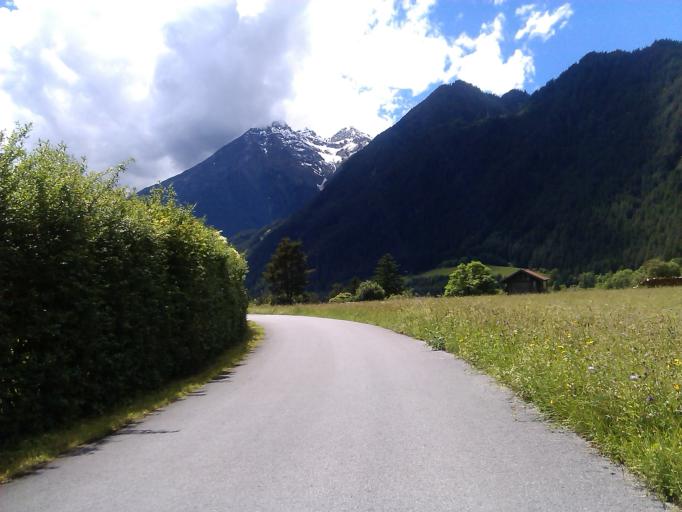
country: AT
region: Tyrol
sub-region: Politischer Bezirk Landeck
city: Pfunds
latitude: 46.9592
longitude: 10.5259
